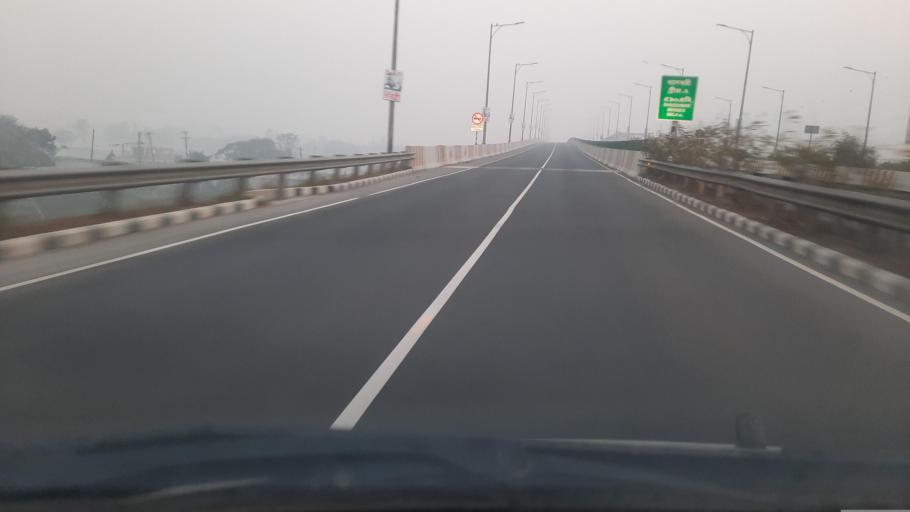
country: BD
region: Dhaka
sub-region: Dhaka
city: Dhaka
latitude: 23.6342
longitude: 90.3451
